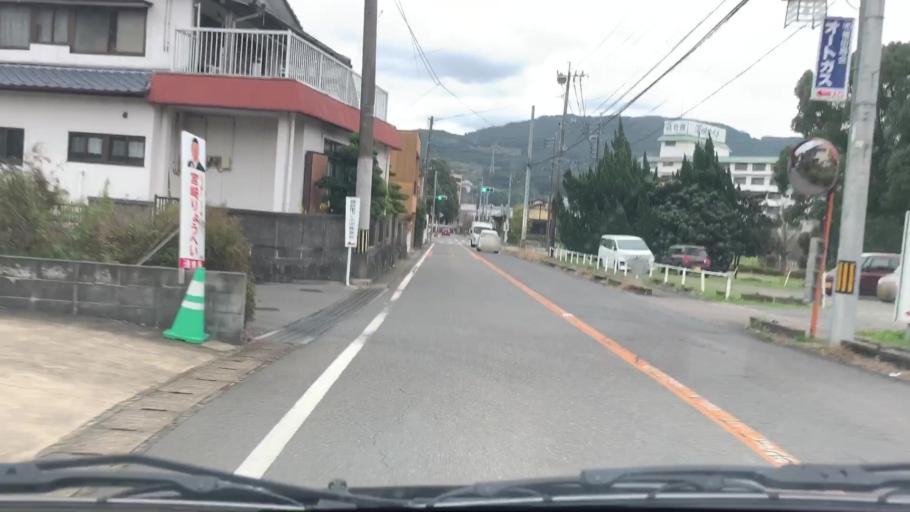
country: JP
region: Saga Prefecture
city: Ureshinomachi-shimojuku
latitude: 33.0999
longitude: 129.9801
